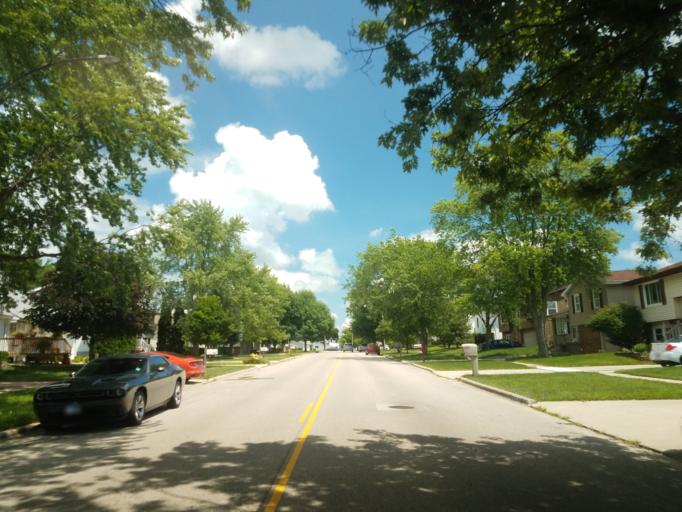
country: US
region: Illinois
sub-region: McLean County
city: Normal
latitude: 40.4962
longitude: -88.9400
